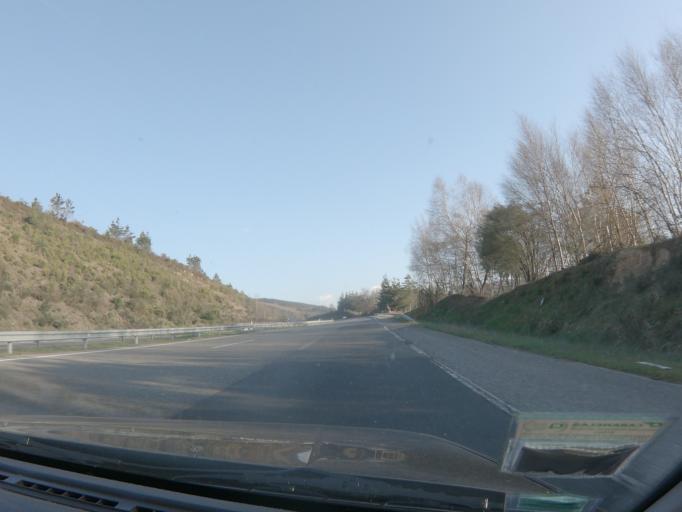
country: ES
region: Galicia
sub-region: Provincia de Lugo
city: Baralla
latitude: 42.9137
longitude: -7.1975
